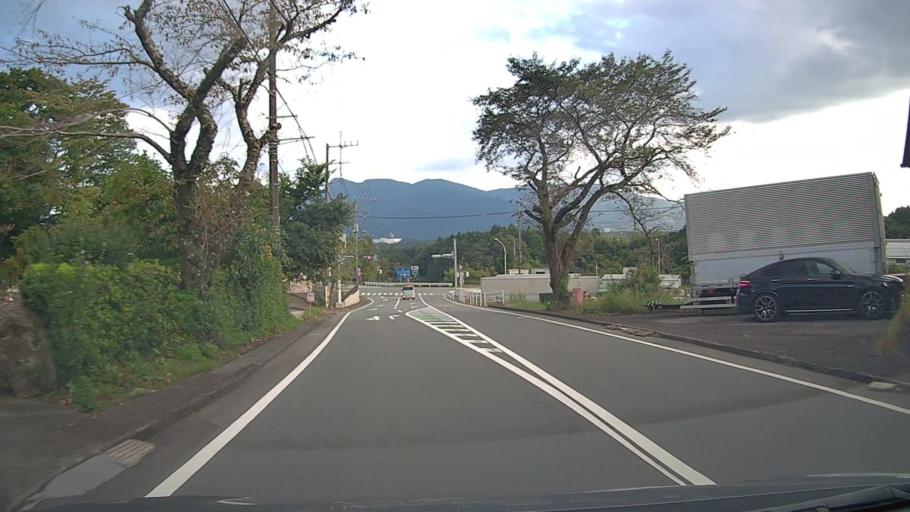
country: JP
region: Shizuoka
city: Gotemba
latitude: 35.3437
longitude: 138.9567
